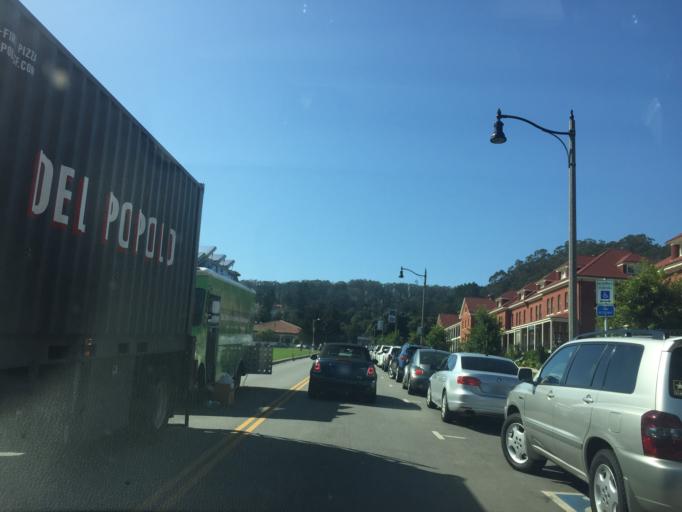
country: US
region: California
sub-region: San Francisco County
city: San Francisco
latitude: 37.8005
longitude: -122.4588
